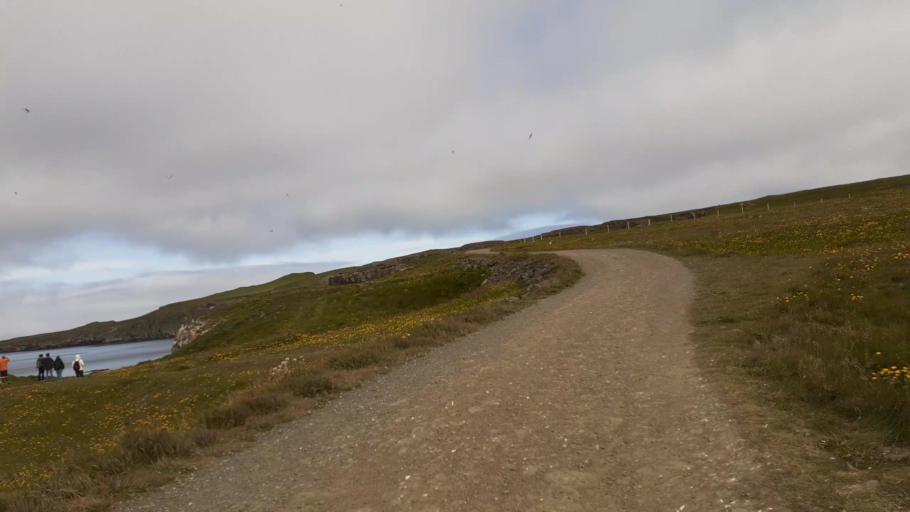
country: IS
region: Northeast
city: Dalvik
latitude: 66.5508
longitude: -18.0251
